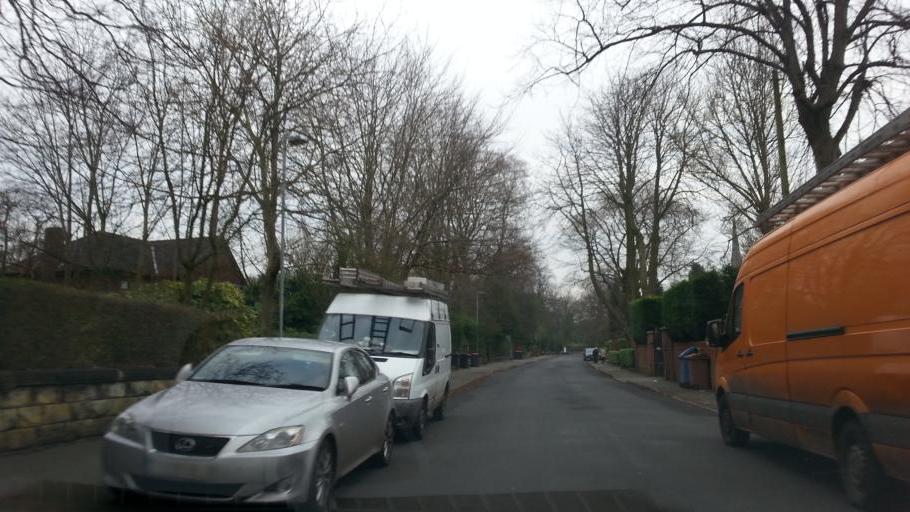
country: GB
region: England
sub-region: Manchester
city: Crumpsall
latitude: 53.5148
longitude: -2.2595
